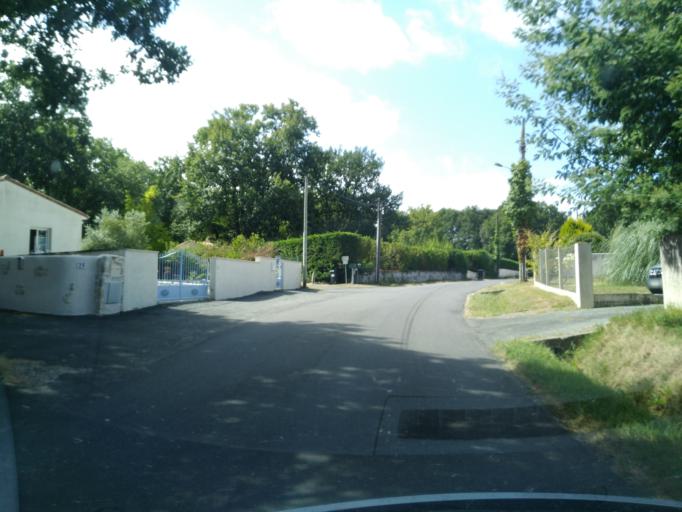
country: FR
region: Poitou-Charentes
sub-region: Departement de la Charente-Maritime
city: Breuillet
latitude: 45.6878
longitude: -1.0736
